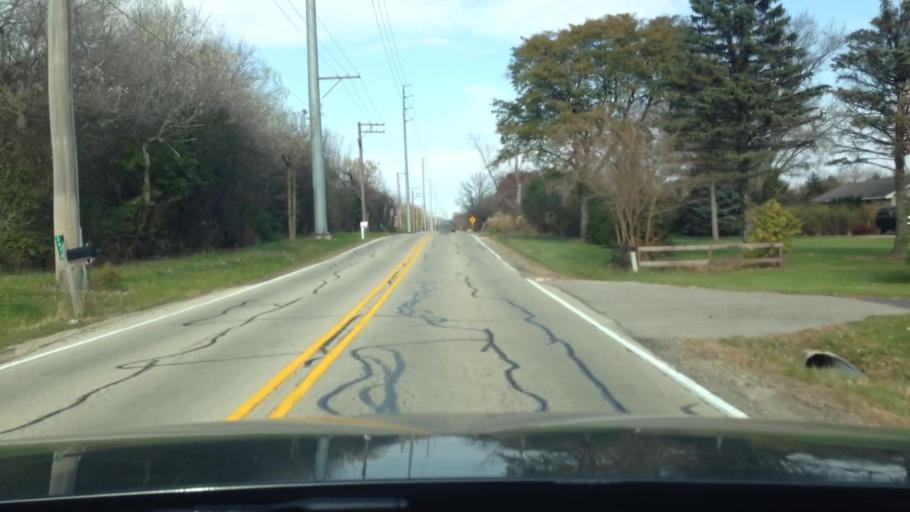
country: US
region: Illinois
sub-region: McHenry County
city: Woodstock
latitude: 42.2714
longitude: -88.4525
